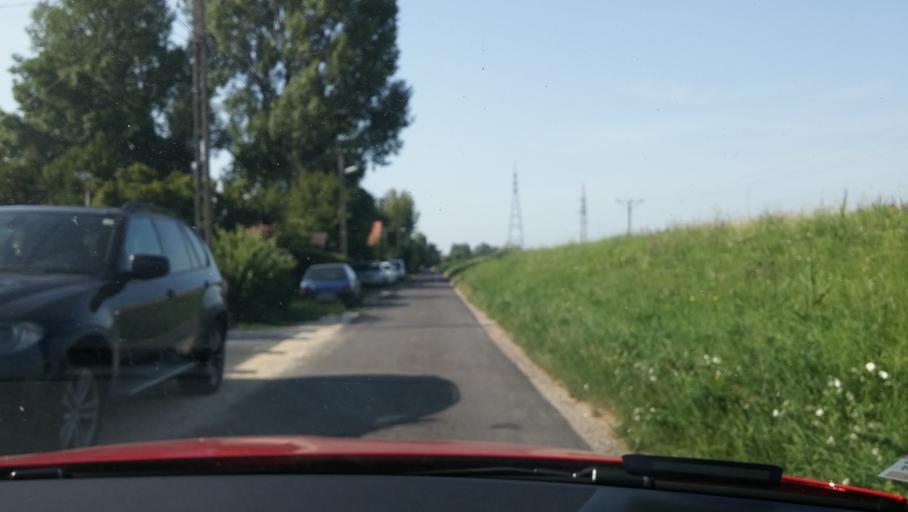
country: HU
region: Pest
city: Rackeve
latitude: 47.1830
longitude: 18.9477
